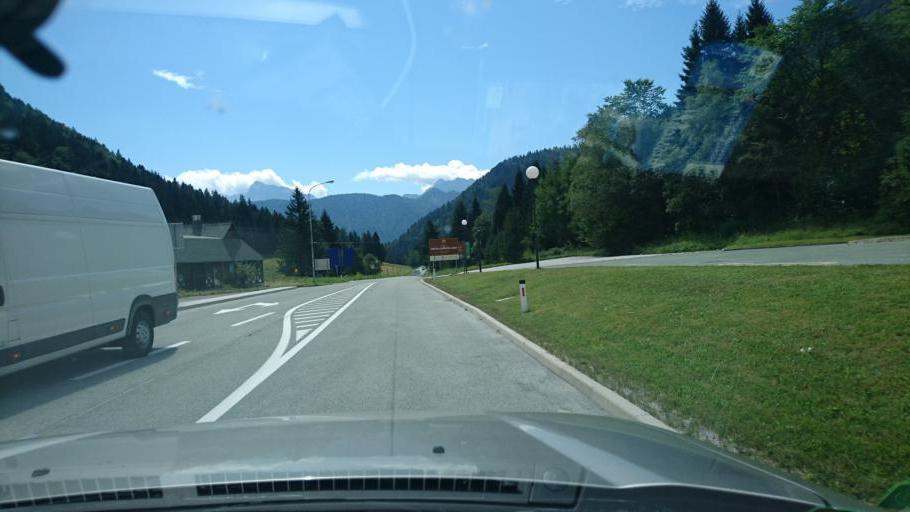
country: AT
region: Carinthia
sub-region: Politischer Bezirk Villach Land
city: Arnoldstein
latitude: 46.5167
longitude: 13.7513
